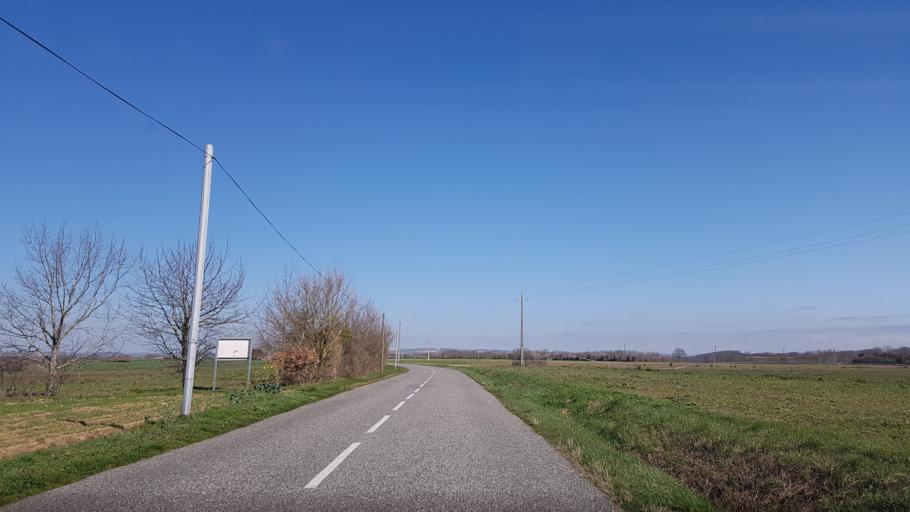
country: FR
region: Languedoc-Roussillon
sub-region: Departement de l'Aude
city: Belpech
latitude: 43.1566
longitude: 1.7077
